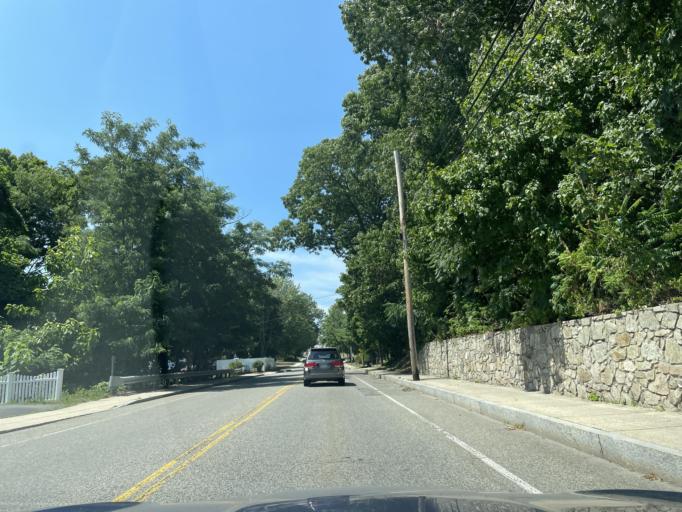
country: US
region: Massachusetts
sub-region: Norfolk County
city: Randolph
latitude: 42.1598
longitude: -71.0368
